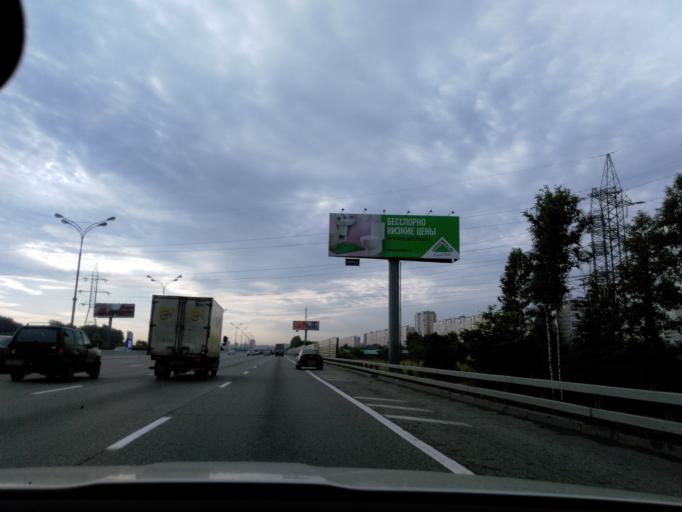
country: RU
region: Moscow
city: Lianozovo
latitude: 55.9051
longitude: 37.6050
